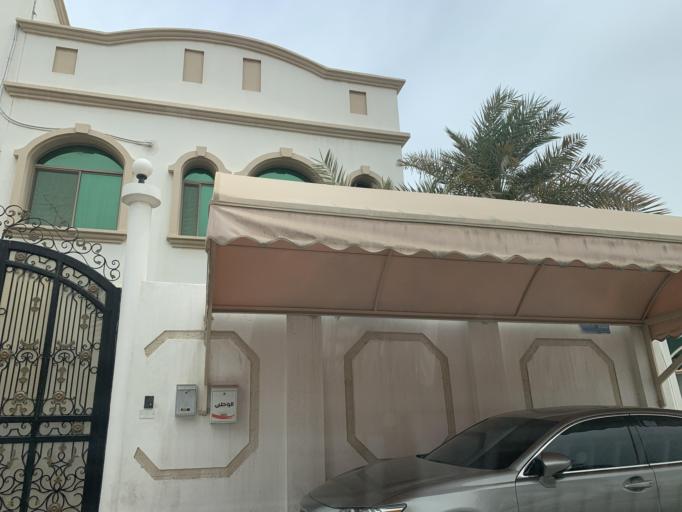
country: BH
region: Northern
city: Ar Rifa'
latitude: 26.1299
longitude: 50.5638
